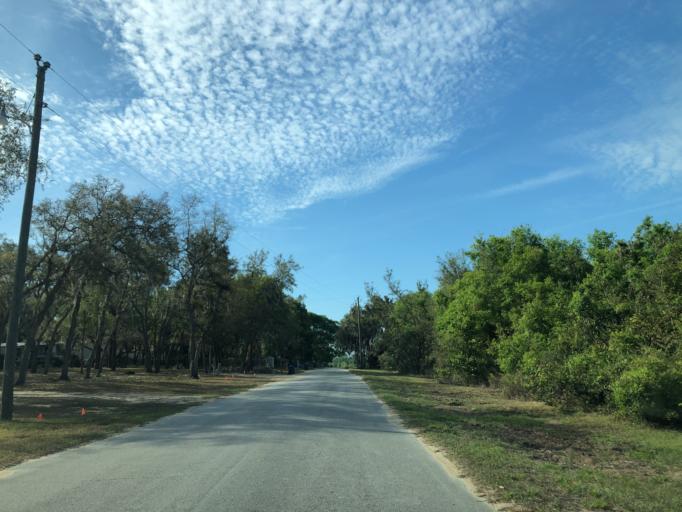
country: US
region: Florida
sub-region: Lake County
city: Astatula
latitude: 28.7130
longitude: -81.7413
